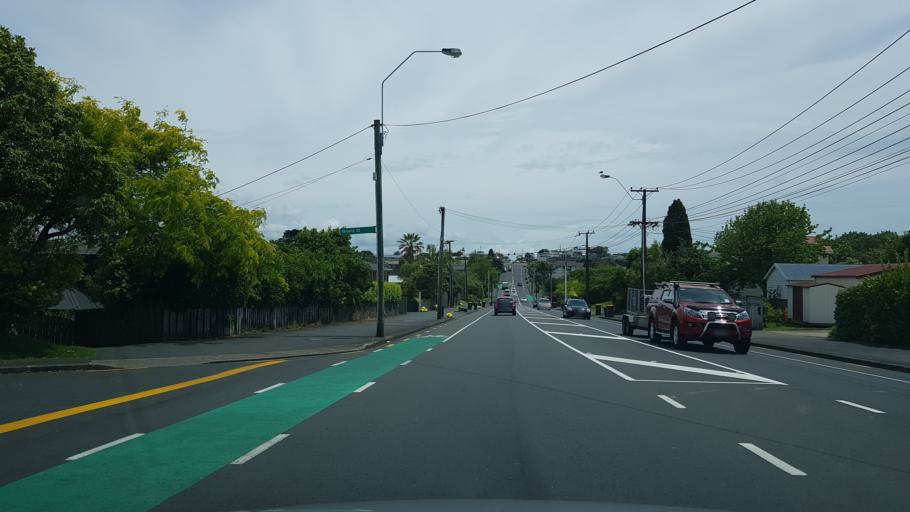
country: NZ
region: Auckland
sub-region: Auckland
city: North Shore
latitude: -36.8125
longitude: 174.7921
